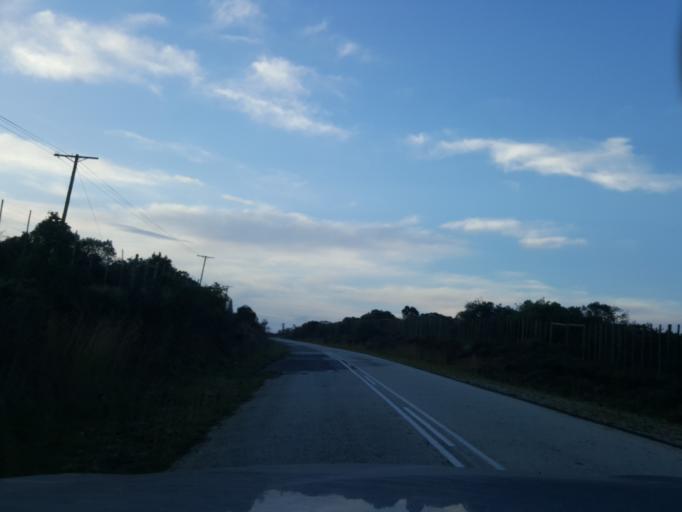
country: ZA
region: Eastern Cape
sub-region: Cacadu District Municipality
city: Grahamstown
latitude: -33.3947
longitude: 26.4752
